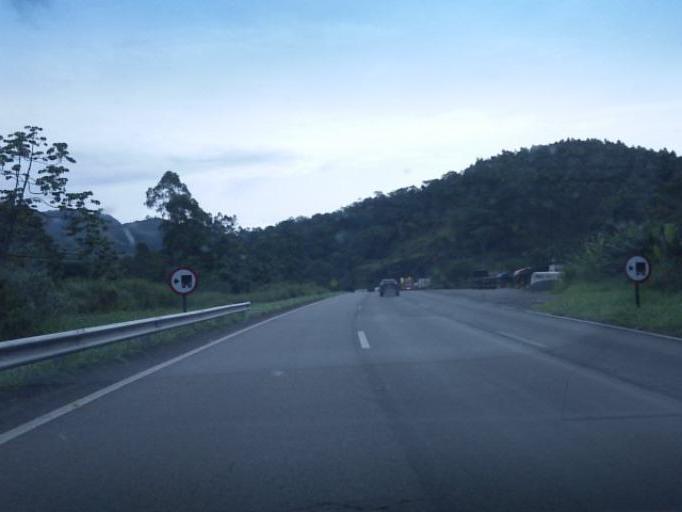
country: BR
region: Sao Paulo
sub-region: Cajati
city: Cajati
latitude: -24.7939
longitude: -48.2116
